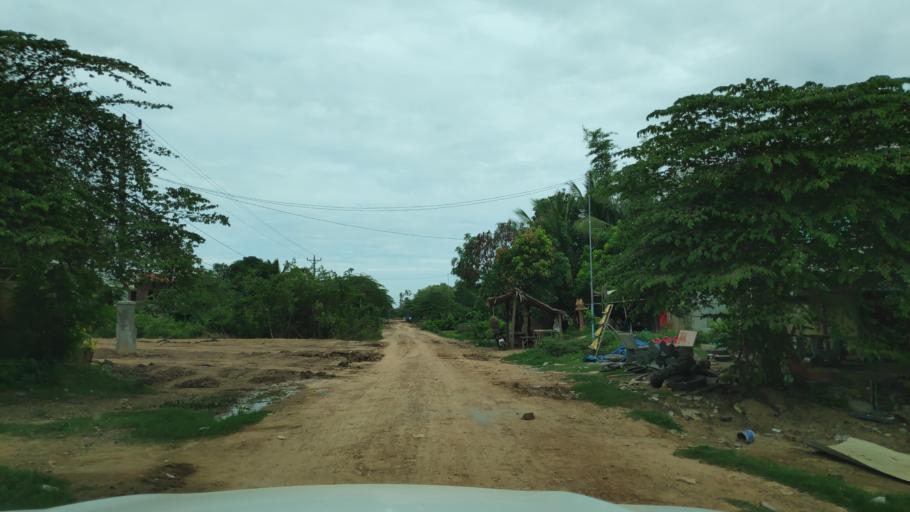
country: KH
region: Kampong Cham
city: Kampong Cham
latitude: 11.9383
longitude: 105.0874
